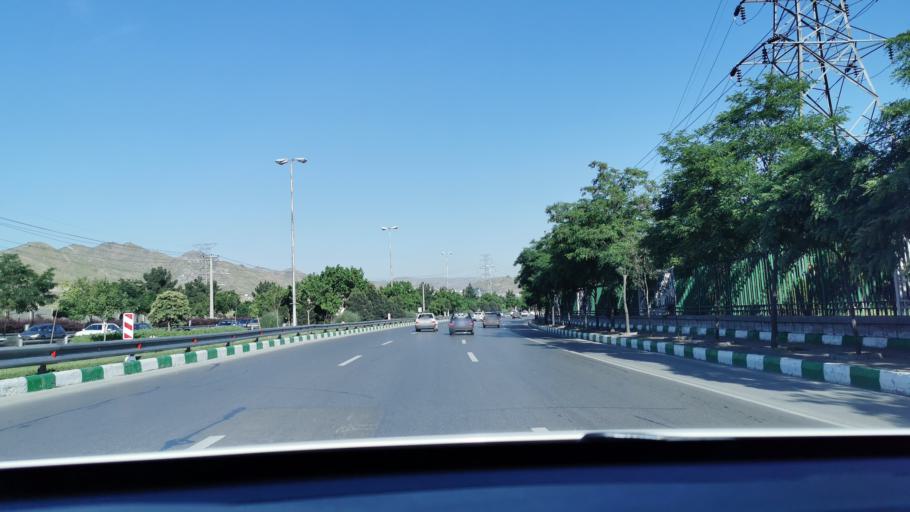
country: IR
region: Razavi Khorasan
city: Mashhad
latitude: 36.2571
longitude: 59.5921
